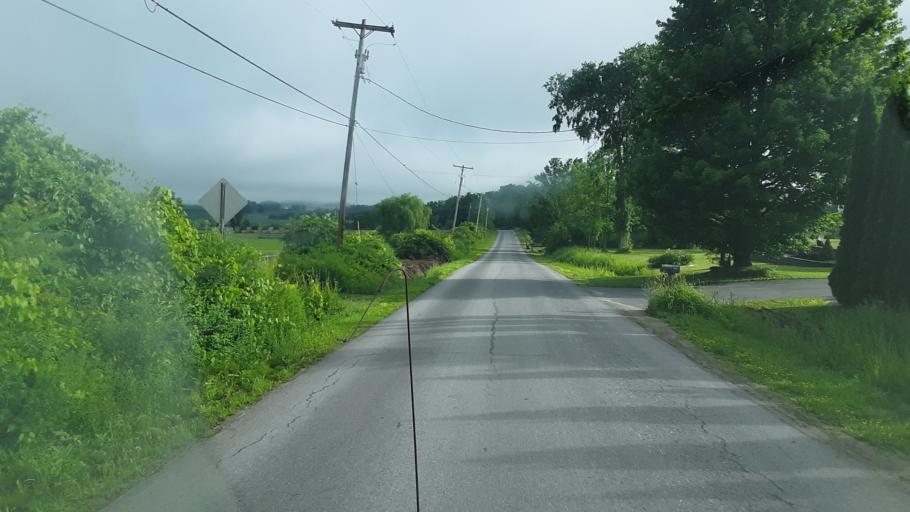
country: US
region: New York
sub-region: Montgomery County
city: Fonda
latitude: 42.8725
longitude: -74.3771
